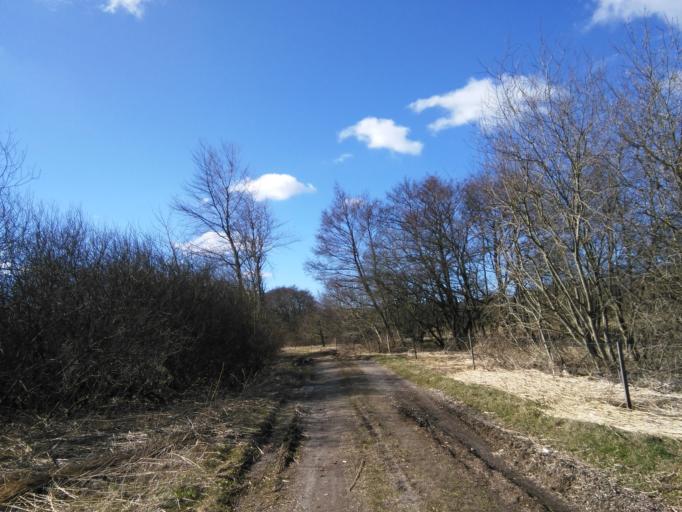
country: DK
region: Central Jutland
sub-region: Skanderborg Kommune
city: Ry
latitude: 56.0462
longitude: 9.7134
